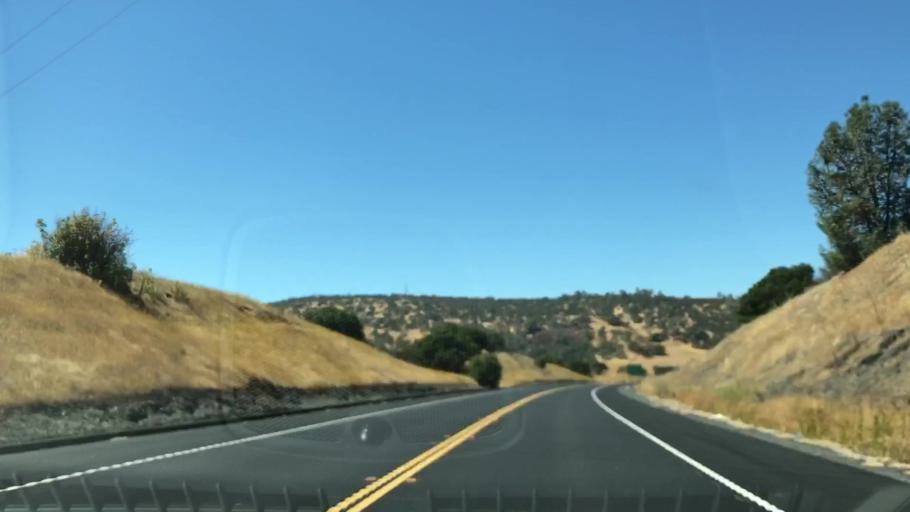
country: US
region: California
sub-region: Calaveras County
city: Copperopolis
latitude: 37.9566
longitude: -120.6822
